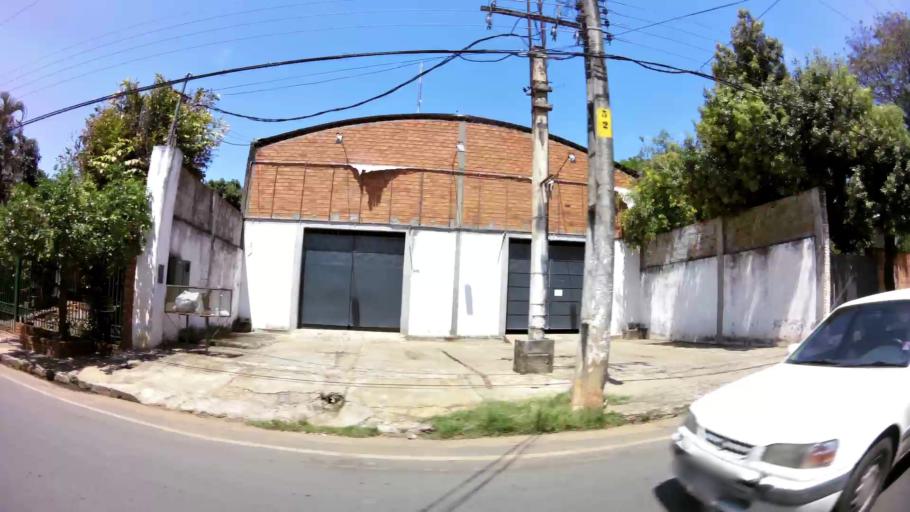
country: PY
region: Central
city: Fernando de la Mora
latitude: -25.3304
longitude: -57.5477
